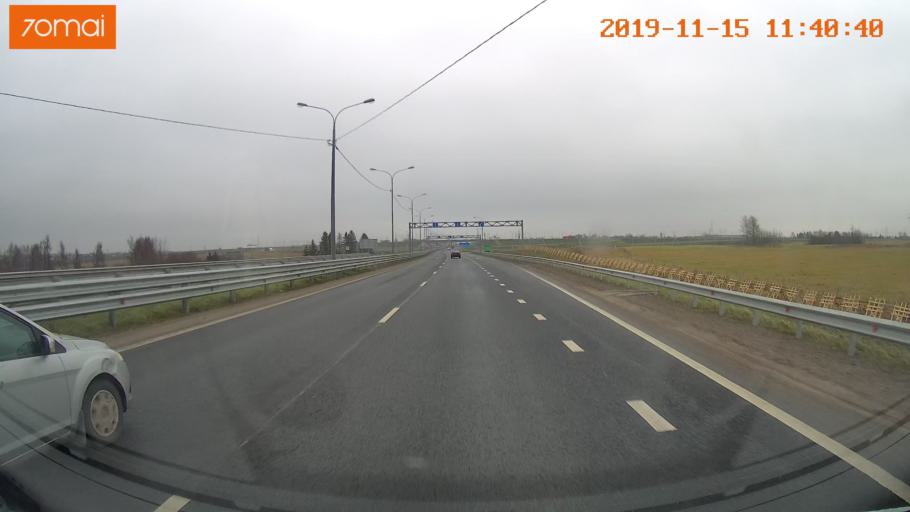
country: RU
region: Vologda
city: Molochnoye
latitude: 59.2127
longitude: 39.7568
